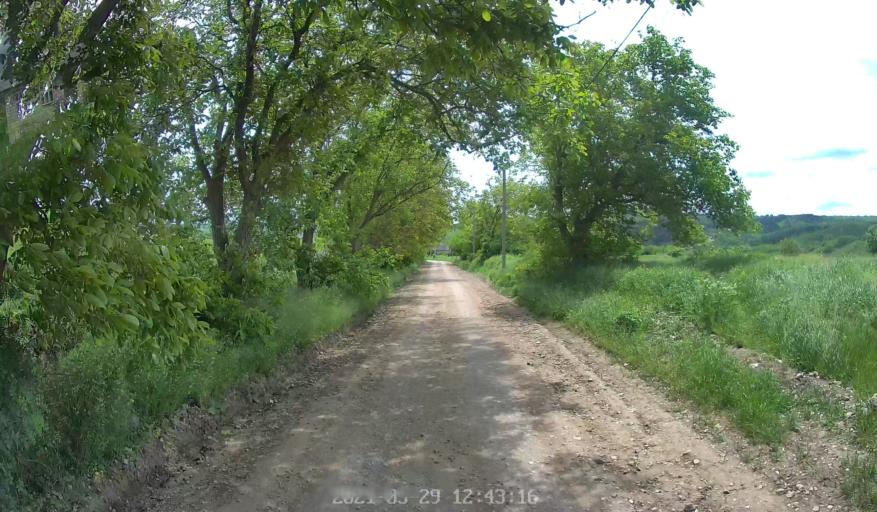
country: MD
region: Hincesti
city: Hincesti
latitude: 46.8750
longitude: 28.6345
